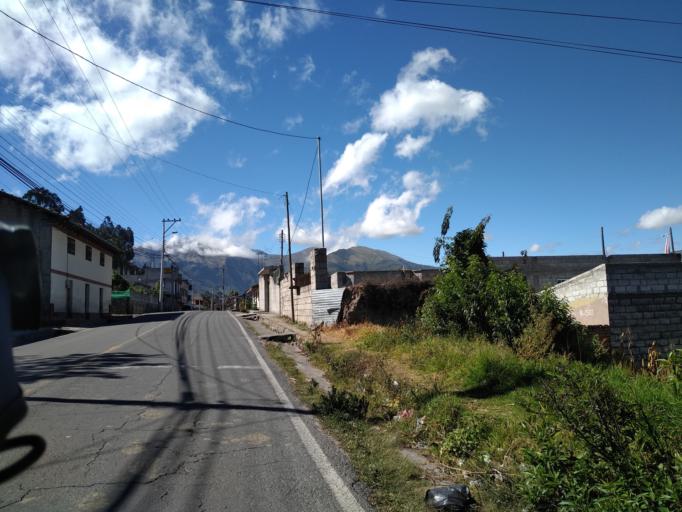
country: EC
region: Imbabura
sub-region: Canton Otavalo
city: Otavalo
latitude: 0.2129
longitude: -78.2116
